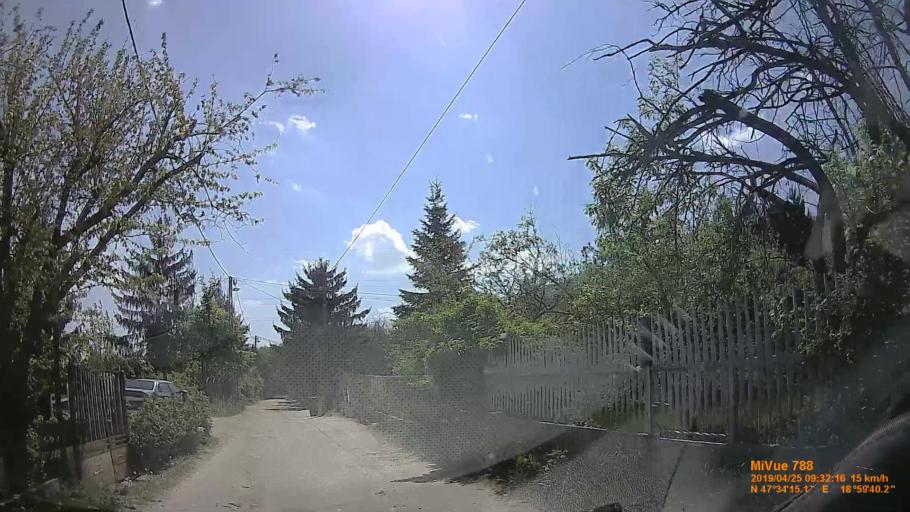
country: HU
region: Pest
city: Urom
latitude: 47.5708
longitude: 18.9946
